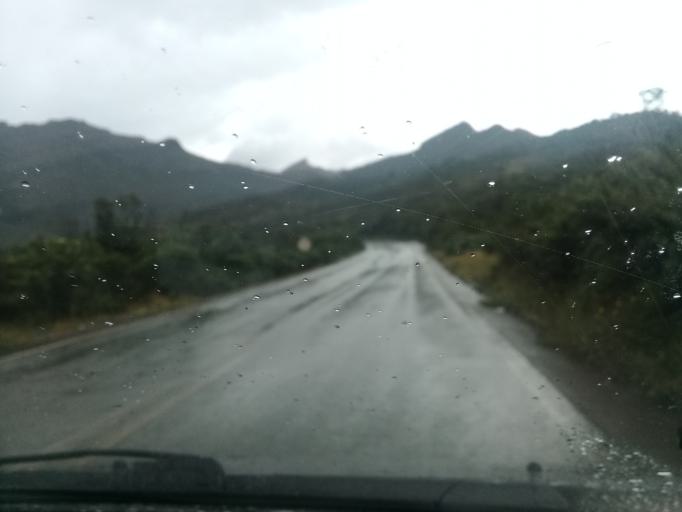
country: CO
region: Cundinamarca
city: Guasca
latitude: 4.8386
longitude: -73.8116
